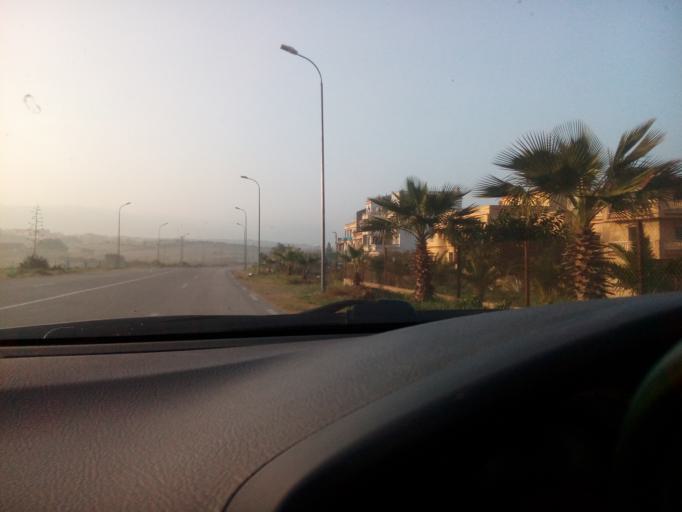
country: DZ
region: Oran
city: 'Ain el Turk
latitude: 35.7308
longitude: -0.8419
